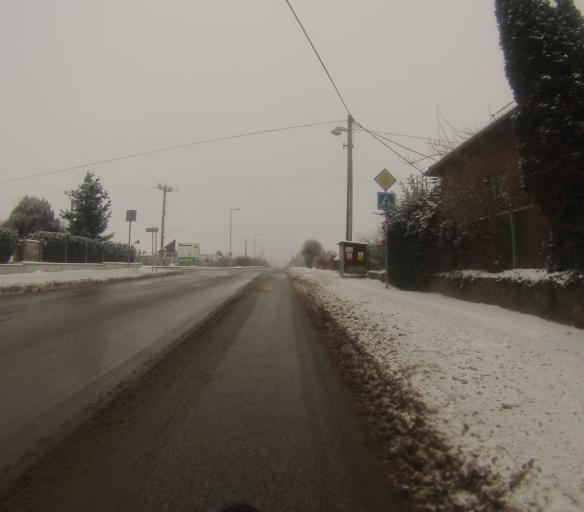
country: CZ
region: South Moravian
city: Troubsko
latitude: 49.1669
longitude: 16.5182
